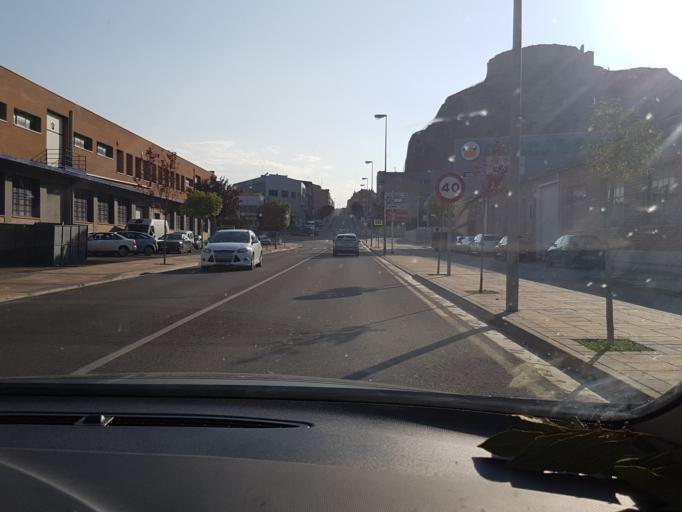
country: ES
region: La Rioja
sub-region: Provincia de La Rioja
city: Arnedo
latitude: 42.2289
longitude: -2.0917
